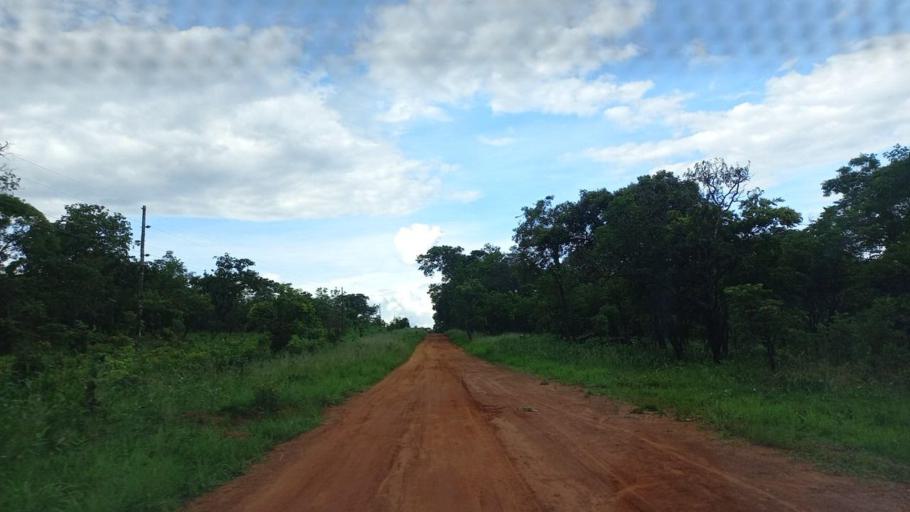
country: ZM
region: North-Western
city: Mwinilunga
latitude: -11.7878
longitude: 24.3730
